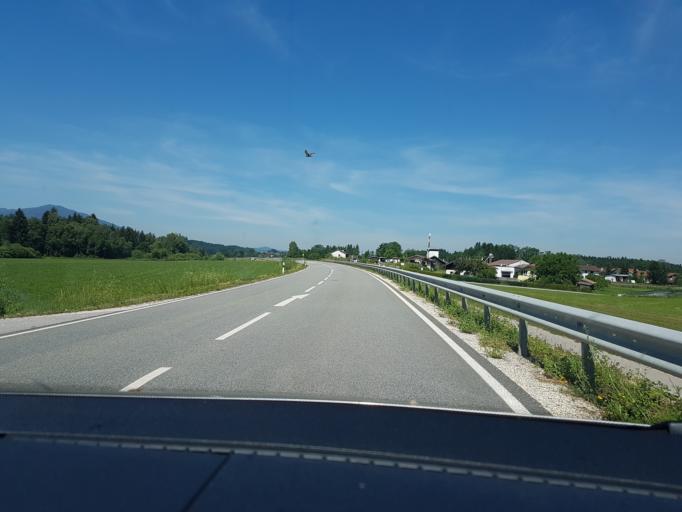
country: DE
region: Bavaria
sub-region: Upper Bavaria
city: Ainring
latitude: 47.8335
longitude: 12.9331
